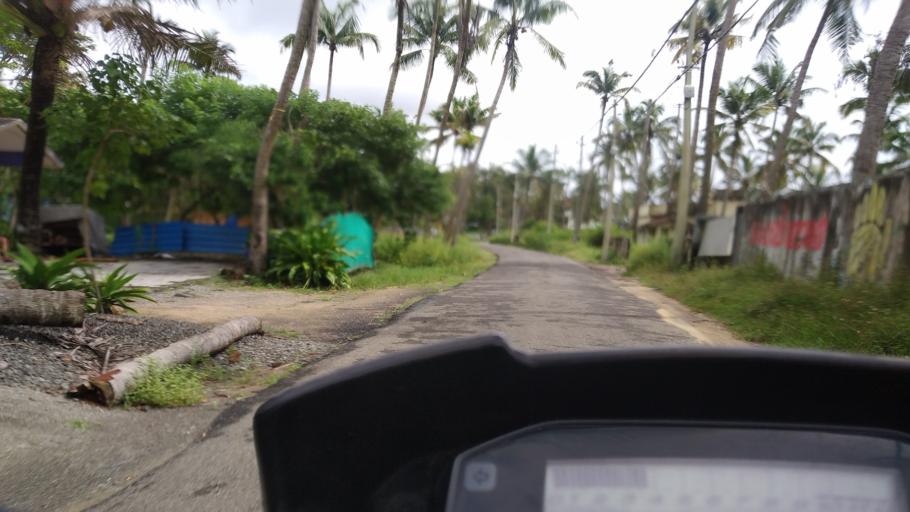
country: IN
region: Kerala
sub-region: Thrissur District
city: Kodungallur
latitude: 10.1648
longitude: 76.1705
